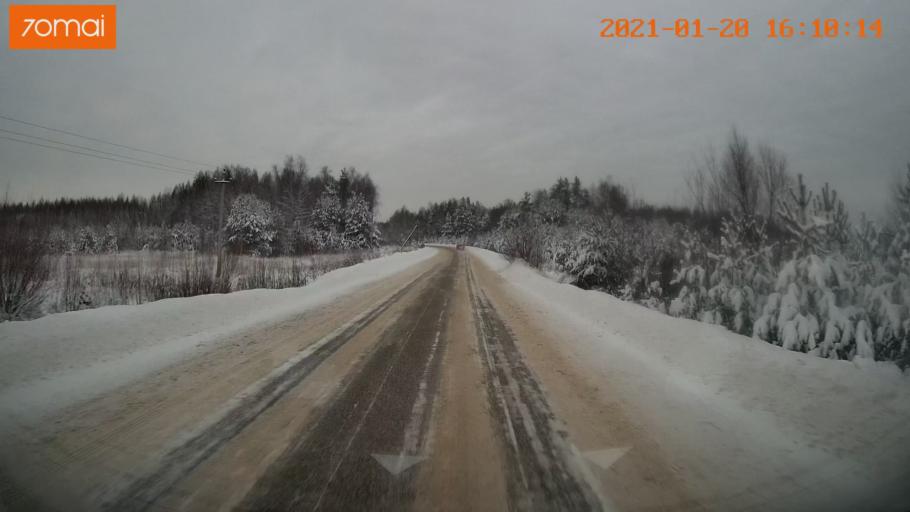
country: RU
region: Vladimir
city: Sudogda
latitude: 56.0899
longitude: 40.7859
